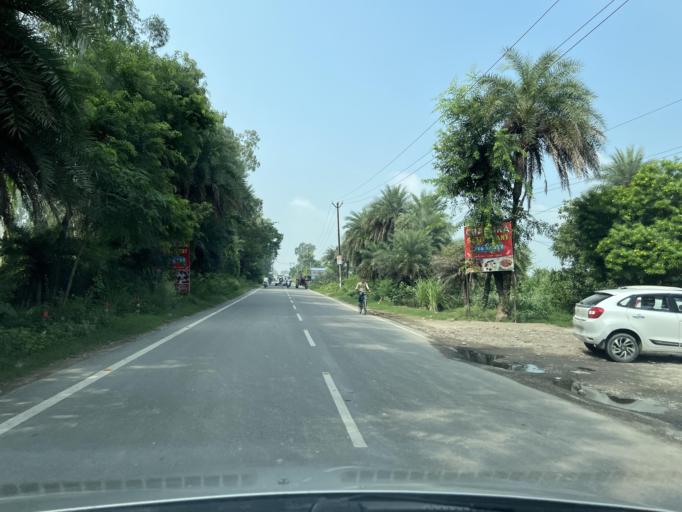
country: IN
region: Uttarakhand
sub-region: Udham Singh Nagar
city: Bazpur
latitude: 29.1684
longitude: 79.1631
